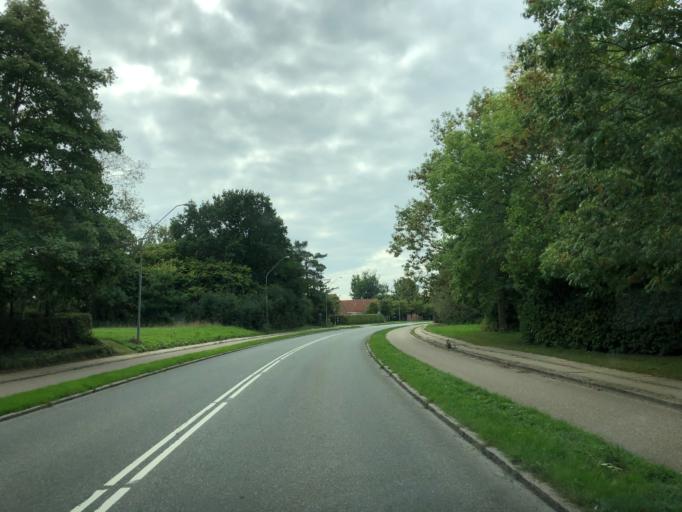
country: DK
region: South Denmark
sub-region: Sonderborg Kommune
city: Sonderborg
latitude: 54.8980
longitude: 9.8163
